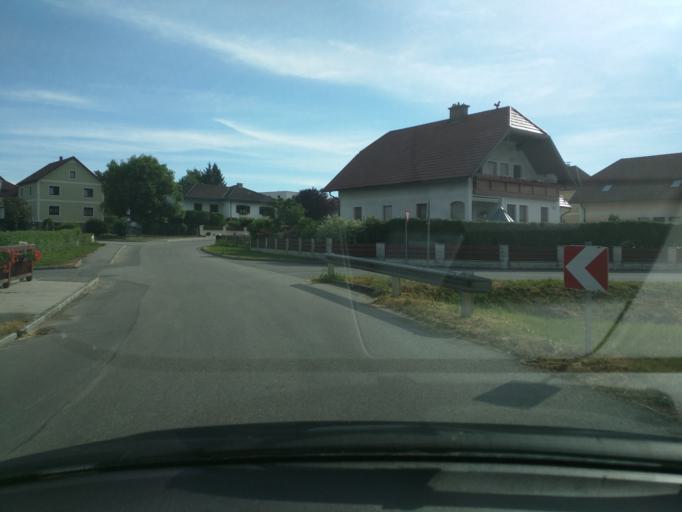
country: AT
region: Lower Austria
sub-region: Politischer Bezirk Melk
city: Erlauf
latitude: 48.1555
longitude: 15.1860
